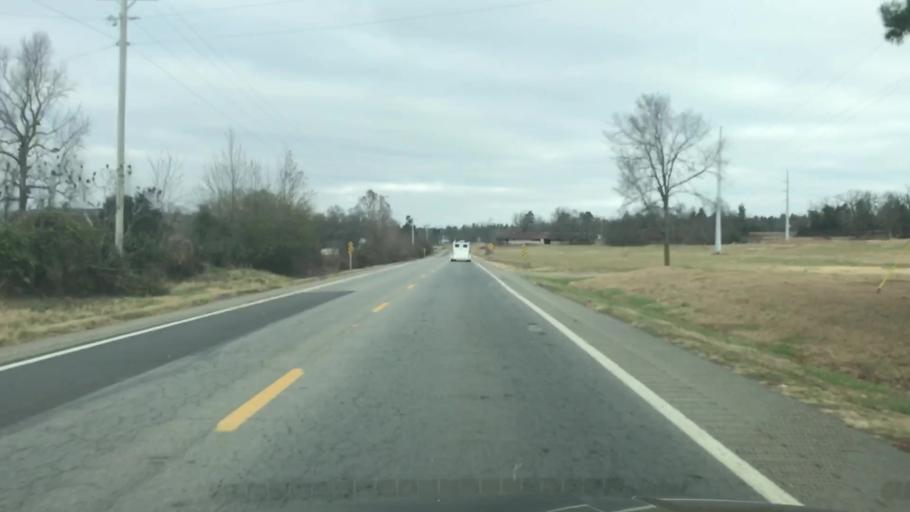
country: US
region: Arkansas
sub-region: Scott County
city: Waldron
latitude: 34.9441
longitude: -94.1033
